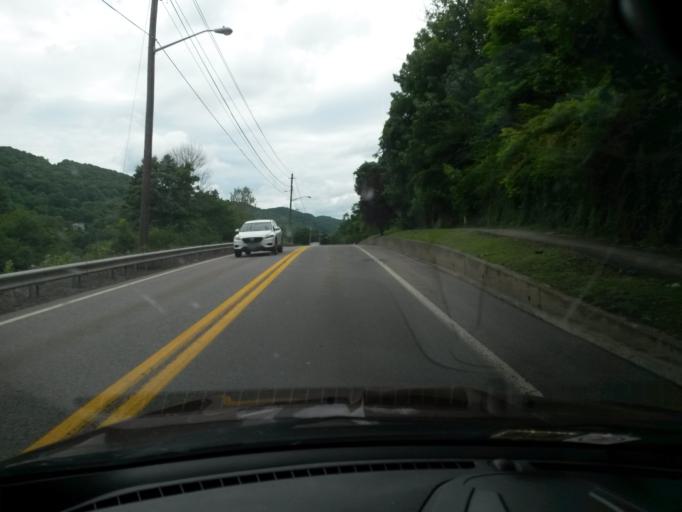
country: US
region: West Virginia
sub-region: Mercer County
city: Bluefield
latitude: 37.2726
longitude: -81.2148
